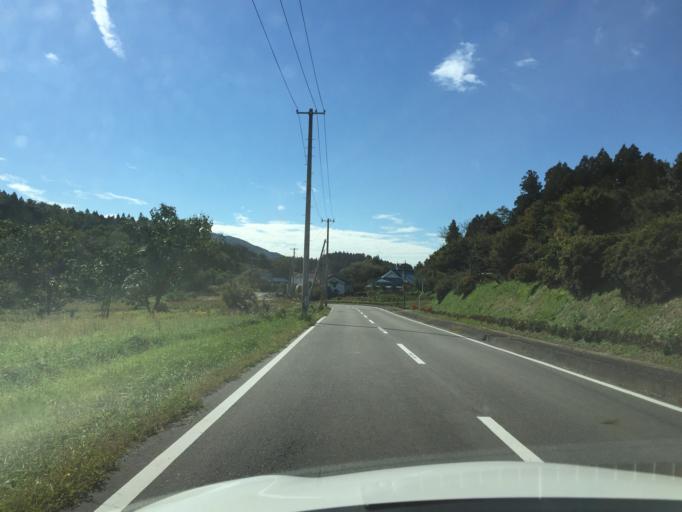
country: JP
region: Fukushima
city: Funehikimachi-funehiki
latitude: 37.4166
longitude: 140.5477
